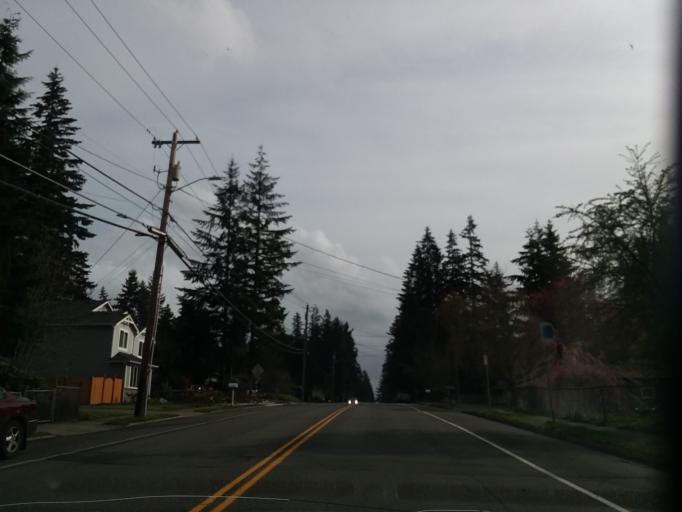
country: US
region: Washington
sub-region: Snohomish County
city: Mountlake Terrace
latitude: 47.7974
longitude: -122.3220
